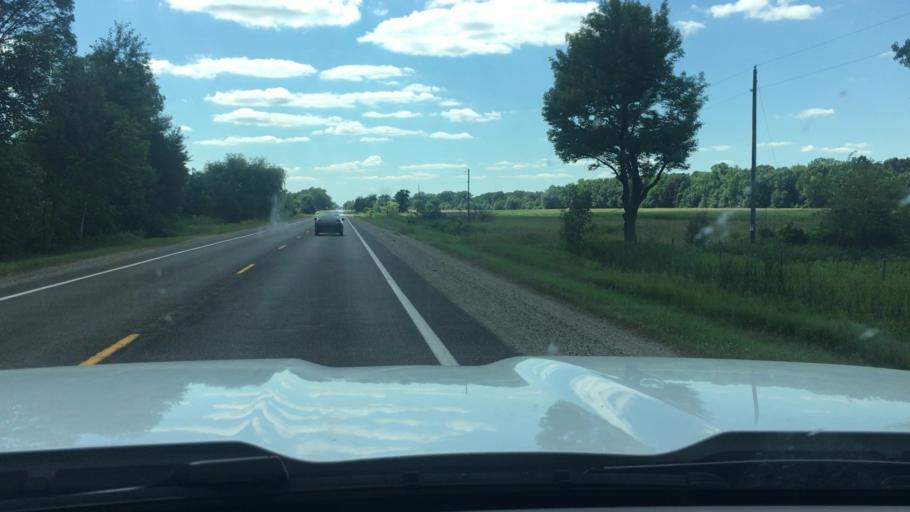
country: US
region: Michigan
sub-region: Clinton County
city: Ovid
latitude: 43.1760
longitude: -84.3977
